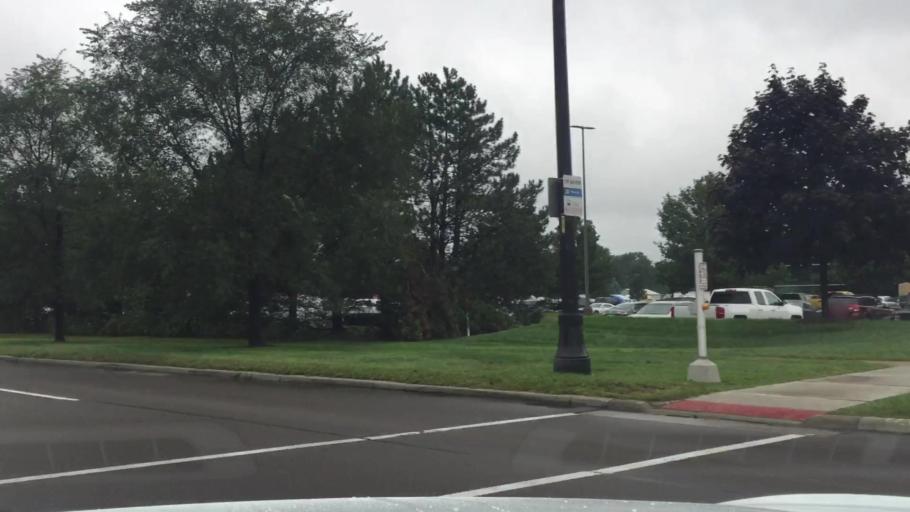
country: US
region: Michigan
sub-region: Wayne County
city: Livonia
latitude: 42.3695
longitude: -83.3233
